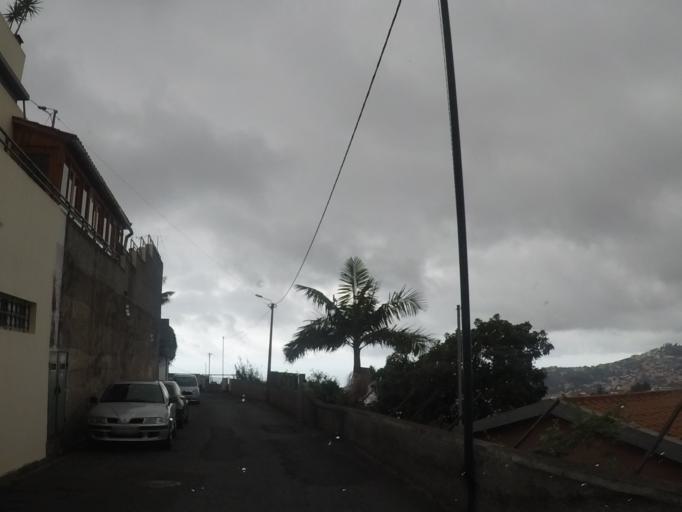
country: PT
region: Madeira
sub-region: Funchal
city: Nossa Senhora do Monte
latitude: 32.6717
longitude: -16.9140
